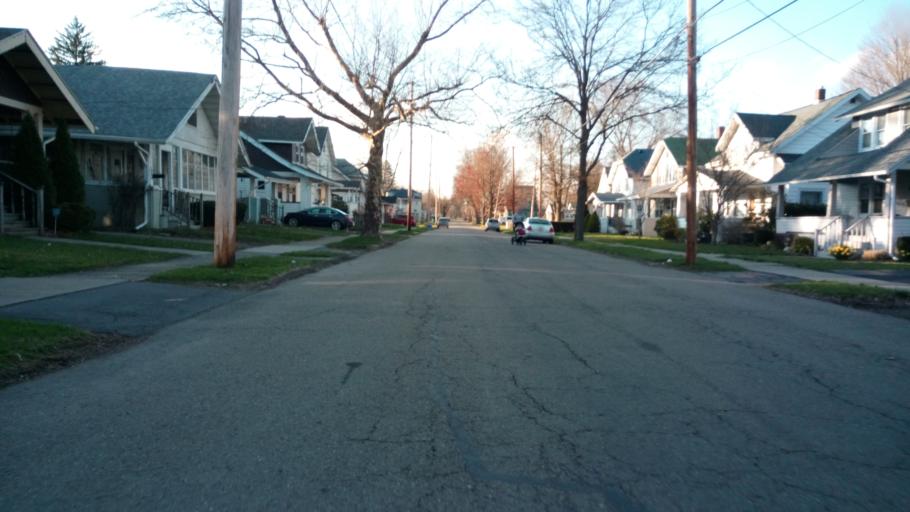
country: US
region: New York
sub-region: Chemung County
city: Elmira
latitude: 42.0807
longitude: -76.7888
